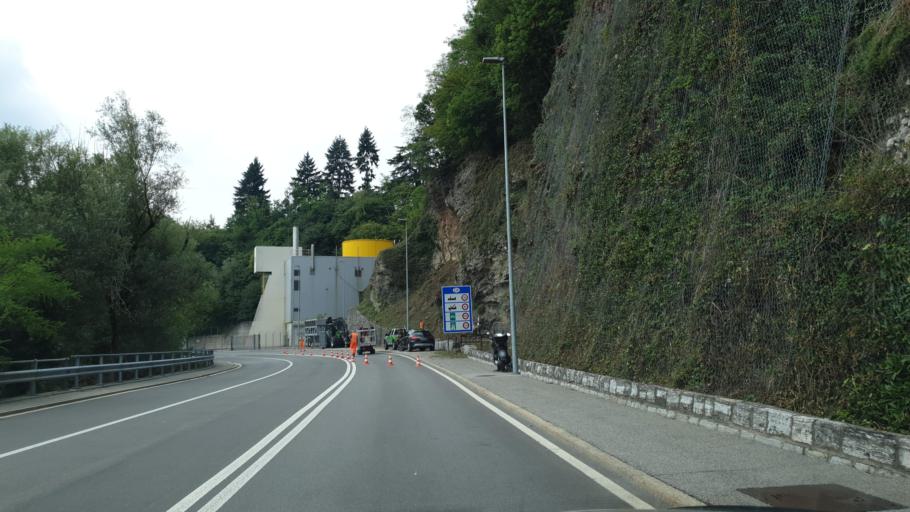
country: CH
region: Ticino
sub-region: Mendrisio District
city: Chiasso
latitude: 45.8418
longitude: 9.0365
